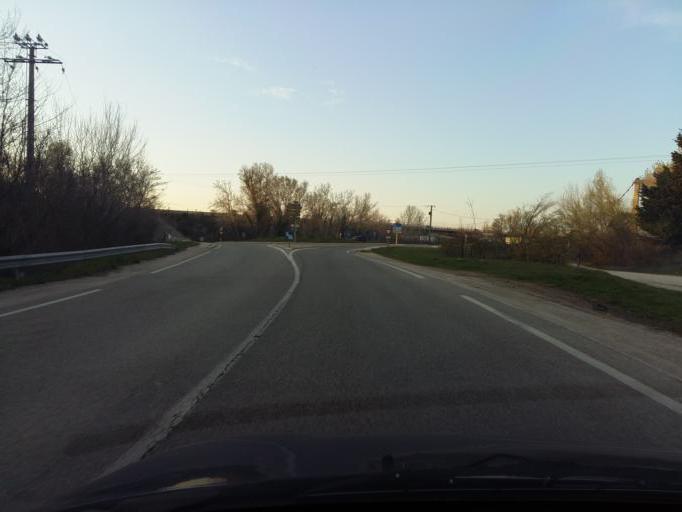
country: FR
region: Languedoc-Roussillon
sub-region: Departement du Gard
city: Montfaucon
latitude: 44.0685
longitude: 4.7677
